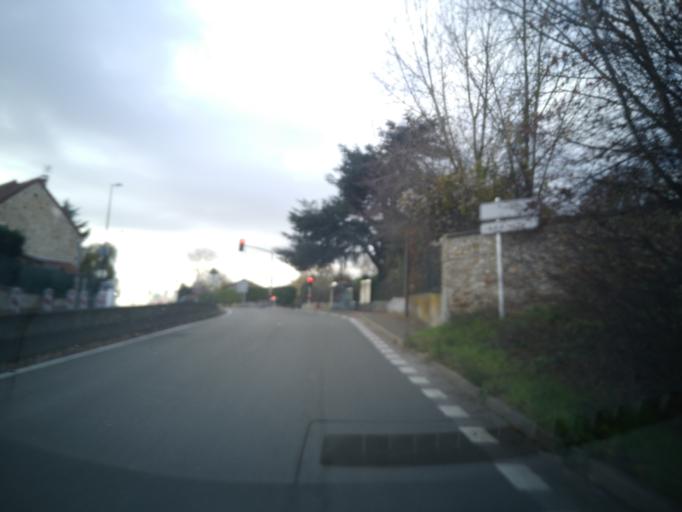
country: FR
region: Ile-de-France
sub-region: Departement des Yvelines
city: Guyancourt
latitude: 48.7756
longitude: 2.0924
